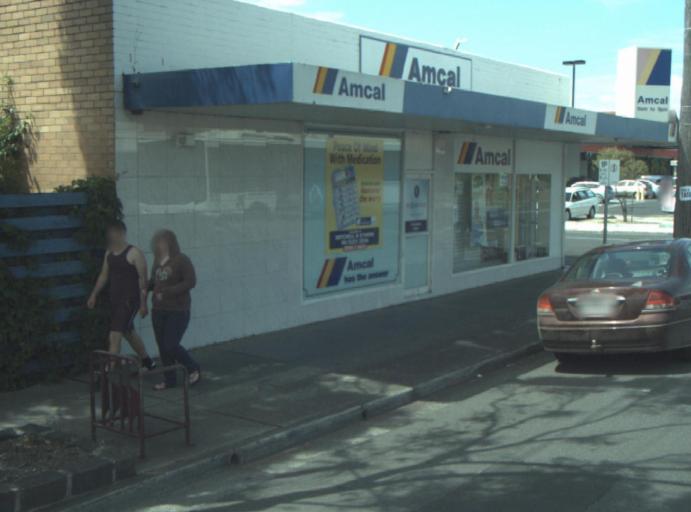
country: AU
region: Victoria
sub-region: Greater Geelong
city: Geelong West
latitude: -38.1382
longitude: 144.3370
